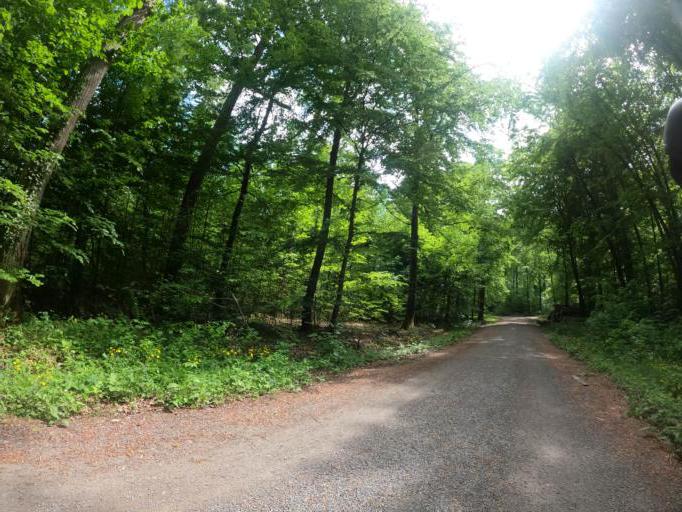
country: DE
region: Baden-Wuerttemberg
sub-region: Regierungsbezirk Stuttgart
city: Holzgerlingen
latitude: 48.6606
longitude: 8.9928
